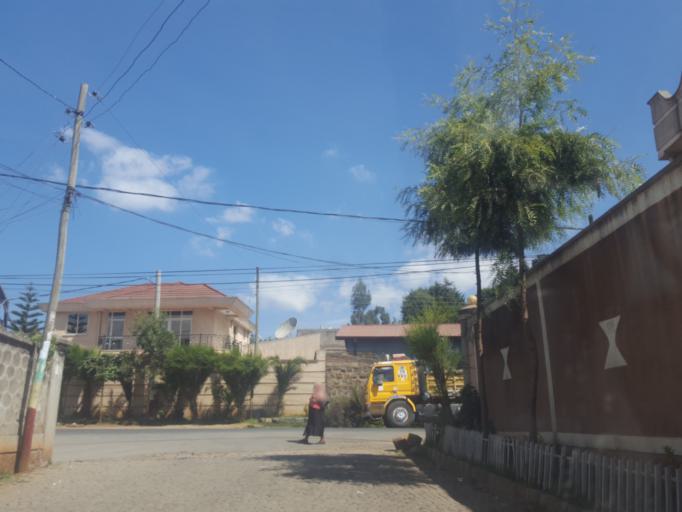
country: ET
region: Adis Abeba
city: Addis Ababa
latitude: 9.0539
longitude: 38.7296
